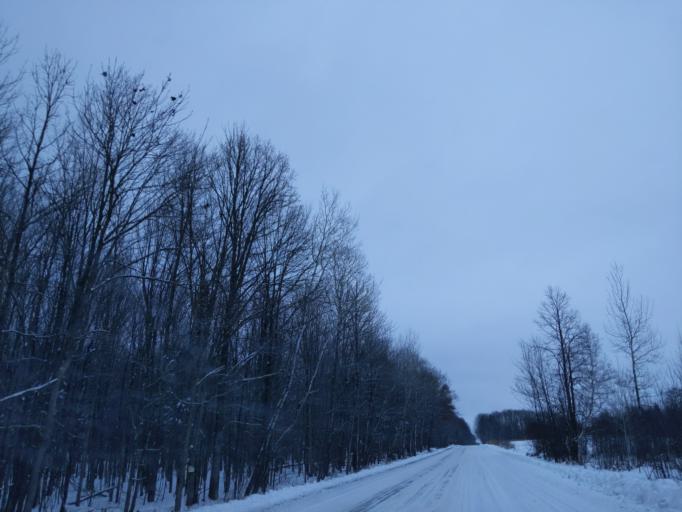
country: US
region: Wisconsin
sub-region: Marathon County
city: Marathon
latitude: 44.7718
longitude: -89.8607
